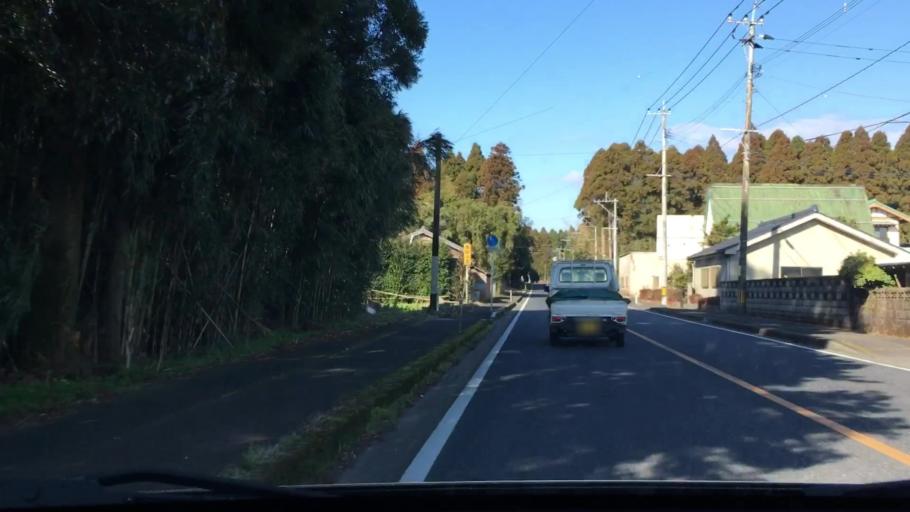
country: JP
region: Kagoshima
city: Kokubu-matsuki
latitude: 31.6712
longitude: 130.8643
